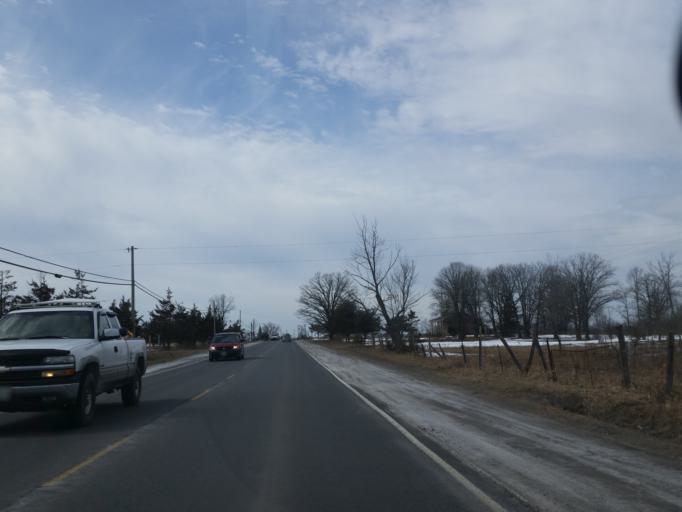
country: CA
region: Ontario
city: Belleville
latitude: 44.1851
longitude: -77.2657
